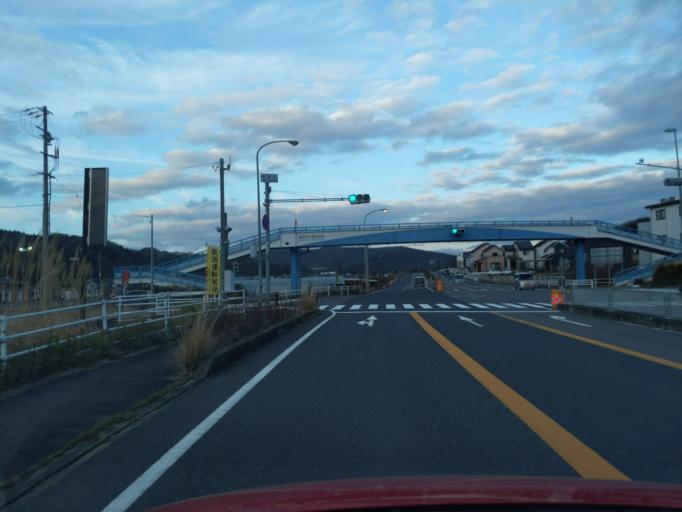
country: JP
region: Gifu
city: Mizunami
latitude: 35.3803
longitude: 137.2680
